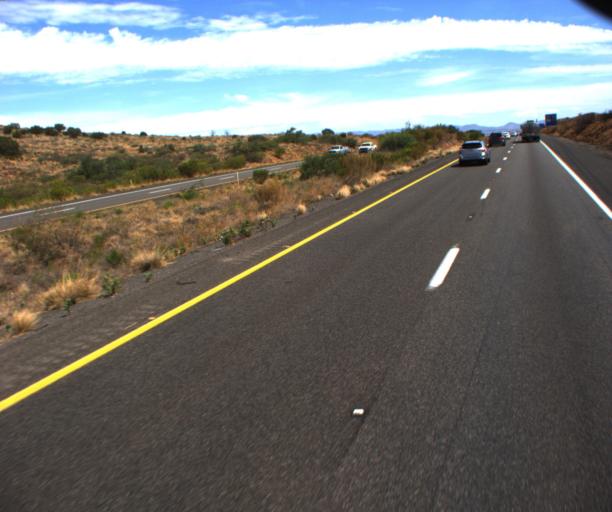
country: US
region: Arizona
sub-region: Yavapai County
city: Cordes Lakes
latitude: 34.3078
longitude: -112.1268
